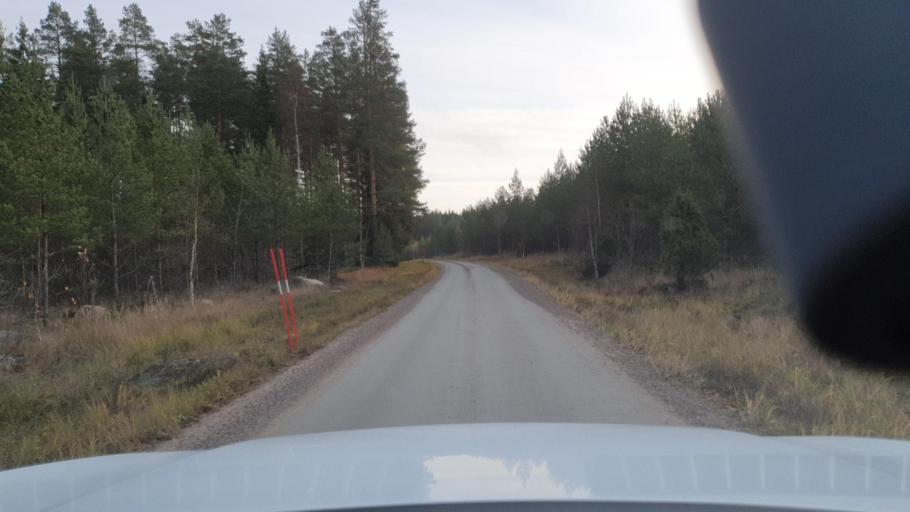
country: SE
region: Uppsala
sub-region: Alvkarleby Kommun
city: AElvkarleby
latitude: 60.4892
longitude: 17.4635
